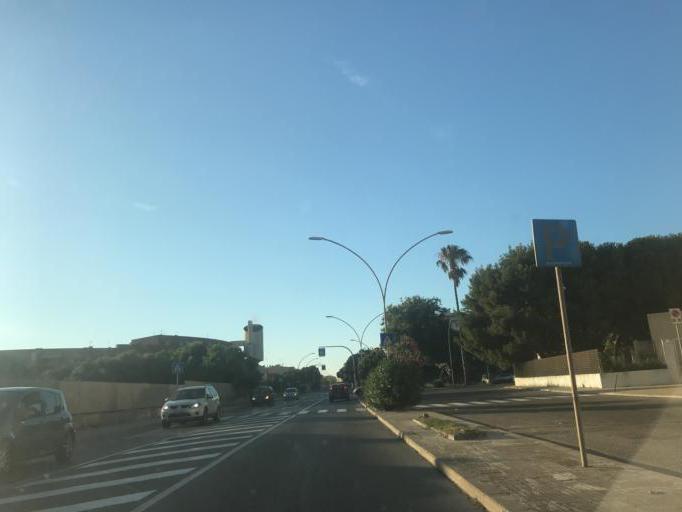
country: IT
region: Sardinia
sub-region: Provincia di Sassari
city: Alghero
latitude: 40.5778
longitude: 8.3194
